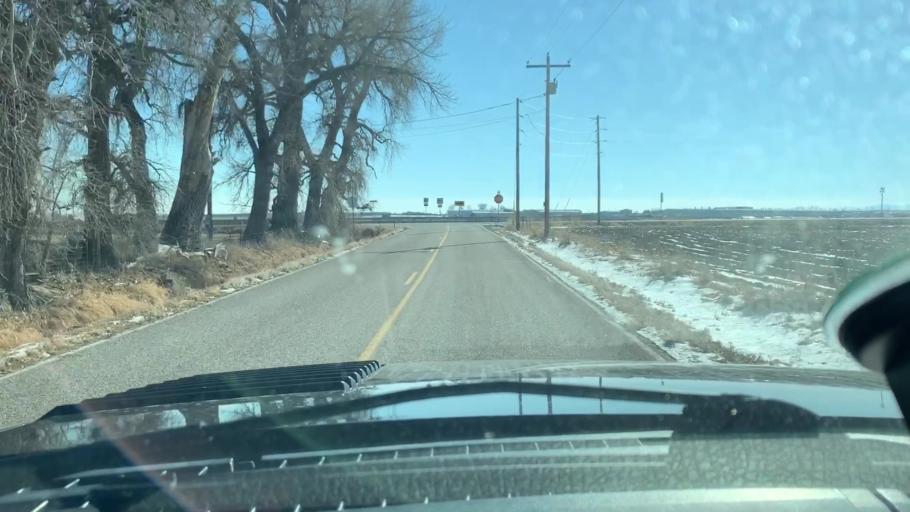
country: US
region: Colorado
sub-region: Weld County
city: Johnstown
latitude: 40.3500
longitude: -104.9835
